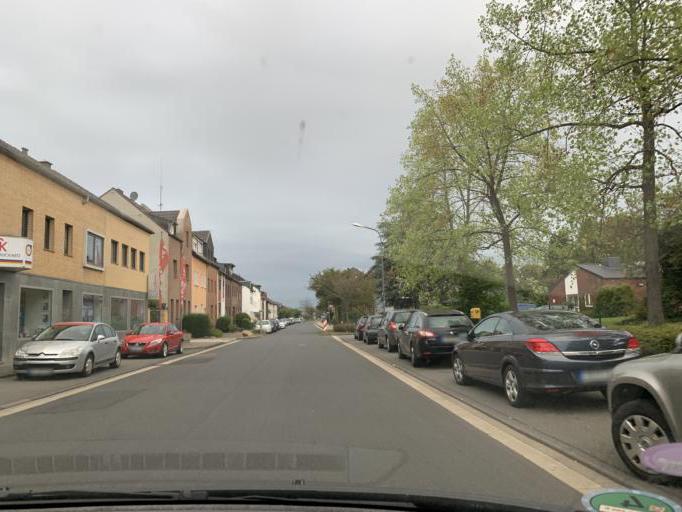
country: DE
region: North Rhine-Westphalia
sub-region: Regierungsbezirk Koln
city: Dueren
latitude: 50.8163
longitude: 6.4441
